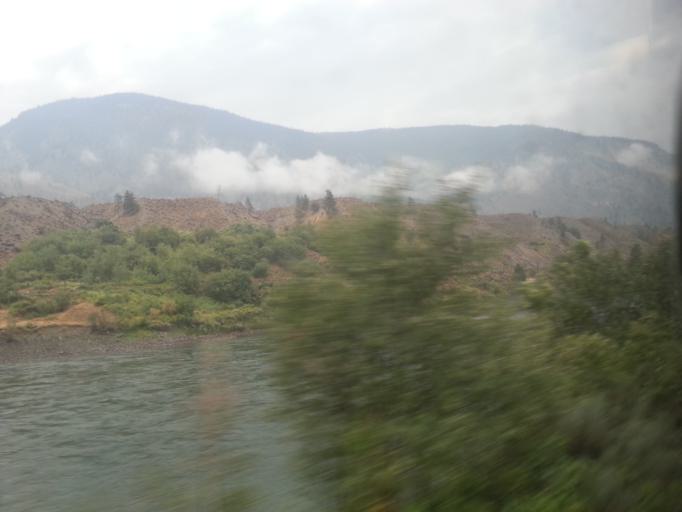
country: CA
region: British Columbia
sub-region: Thompson-Nicola Regional District
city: Ashcroft
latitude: 50.5432
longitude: -121.2895
